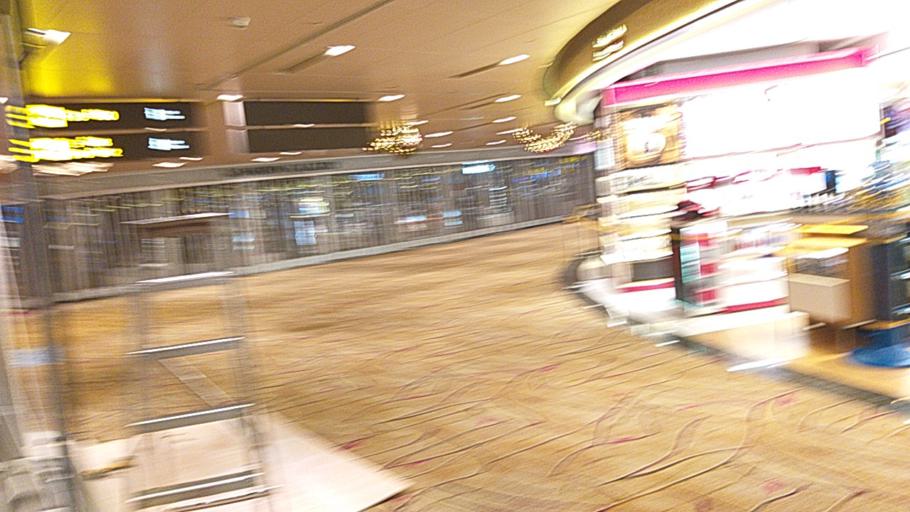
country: SG
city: Singapore
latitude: 1.3548
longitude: 103.9893
